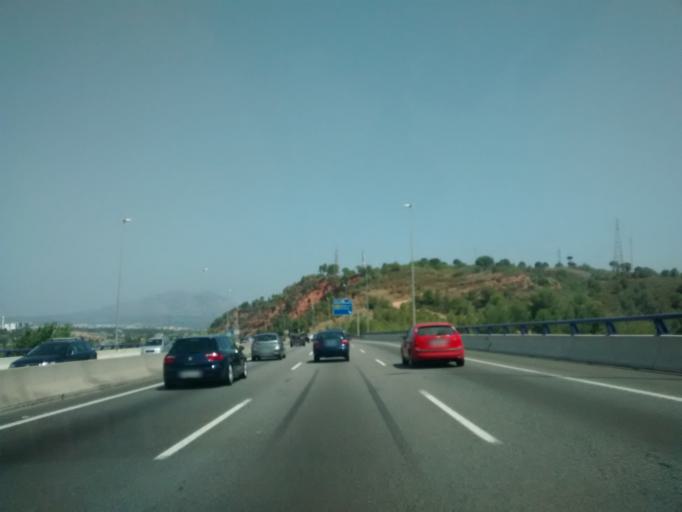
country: ES
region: Catalonia
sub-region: Provincia de Barcelona
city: Martorell
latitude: 41.4839
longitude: 1.9351
